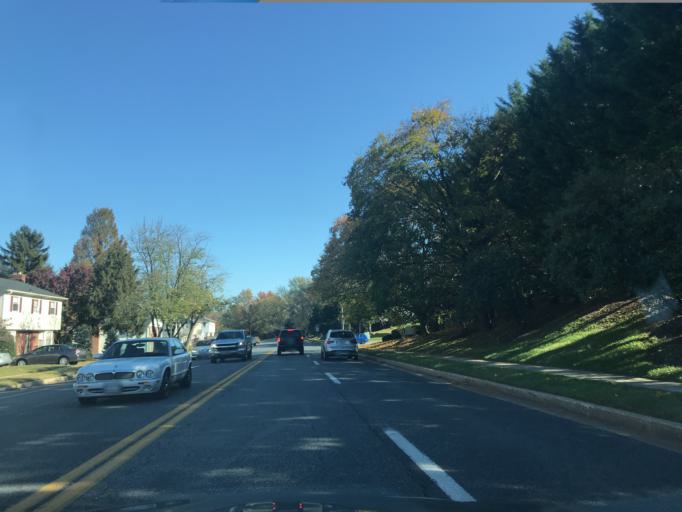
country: US
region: Maryland
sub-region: Baltimore County
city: Cockeysville
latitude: 39.4677
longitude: -76.6292
